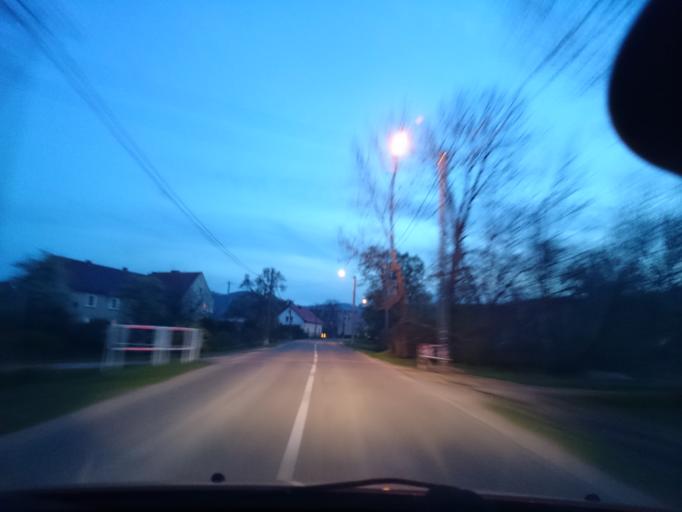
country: PL
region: Lower Silesian Voivodeship
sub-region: Powiat zabkowicki
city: Budzow
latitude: 50.5787
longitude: 16.6870
